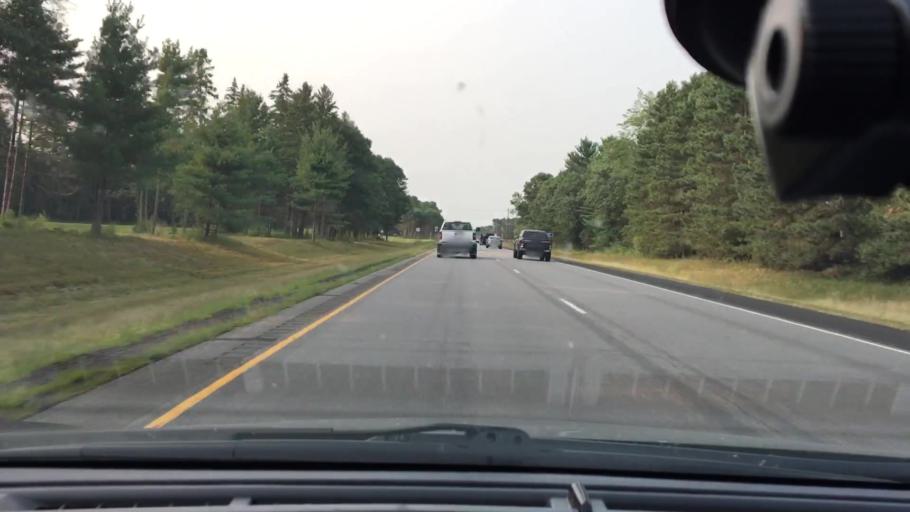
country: US
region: Minnesota
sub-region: Mille Lacs County
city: Princeton
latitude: 45.5166
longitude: -93.5825
